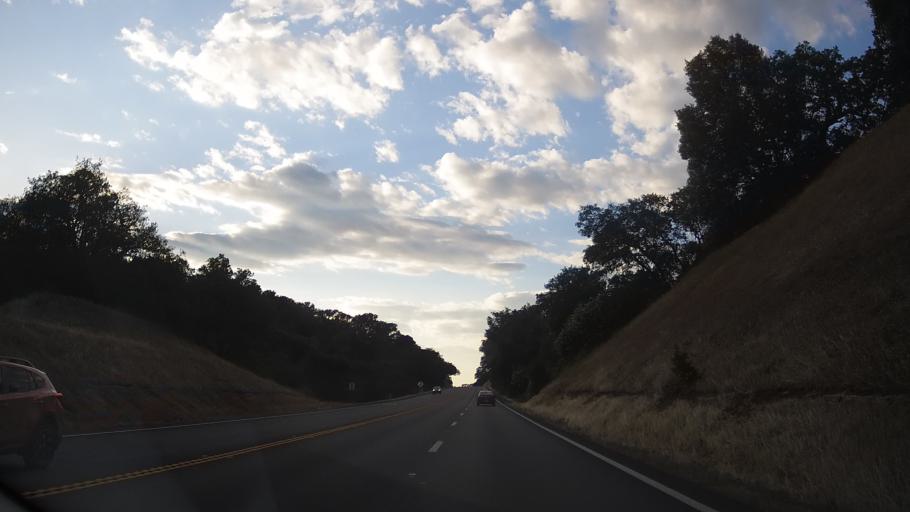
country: US
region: California
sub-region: Mendocino County
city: Talmage
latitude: 39.0062
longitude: -123.1214
